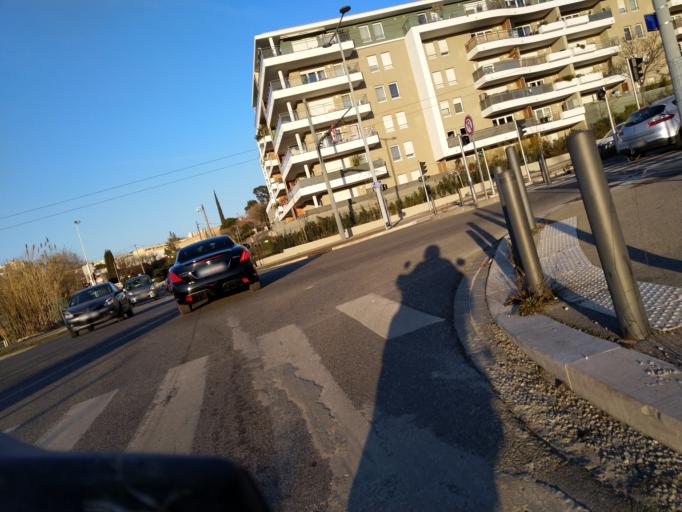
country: FR
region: Provence-Alpes-Cote d'Azur
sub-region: Departement des Bouches-du-Rhone
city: Marseille 12
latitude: 43.2948
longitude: 5.4270
